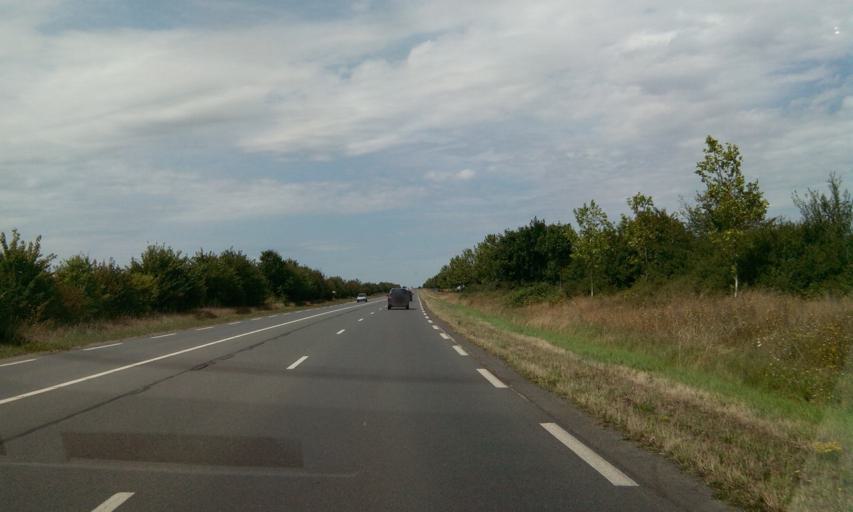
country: FR
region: Poitou-Charentes
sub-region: Departement des Deux-Sevres
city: Vouille
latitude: 46.3011
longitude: -0.3483
